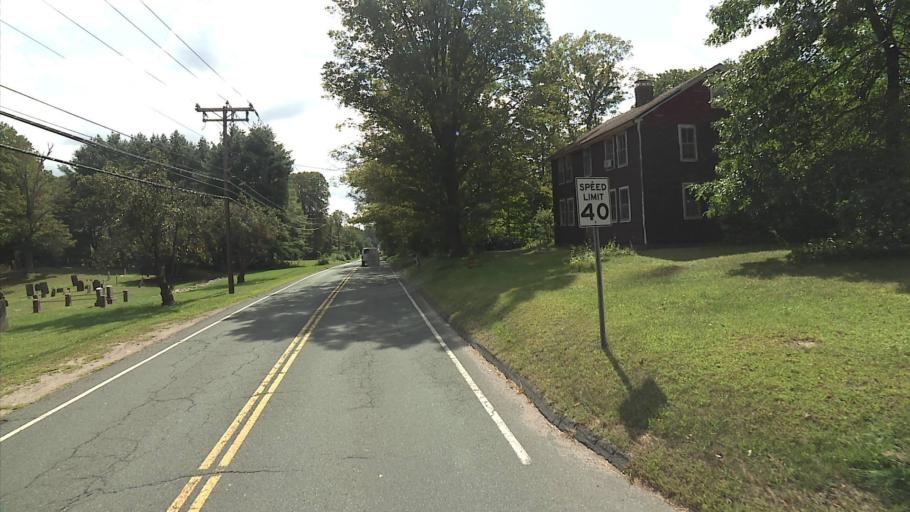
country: US
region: Connecticut
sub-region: Hartford County
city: North Granby
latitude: 41.9842
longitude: -72.8214
